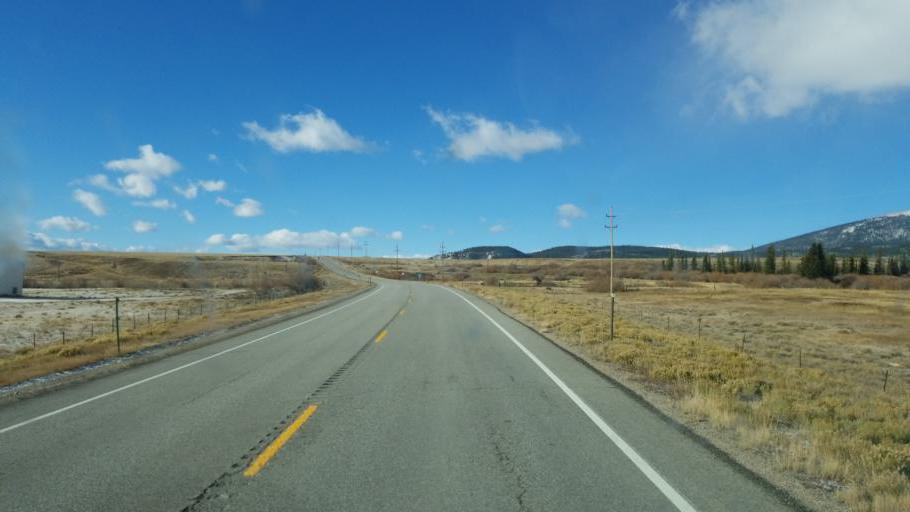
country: US
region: Colorado
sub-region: Park County
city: Fairplay
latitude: 39.3342
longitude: -105.8655
